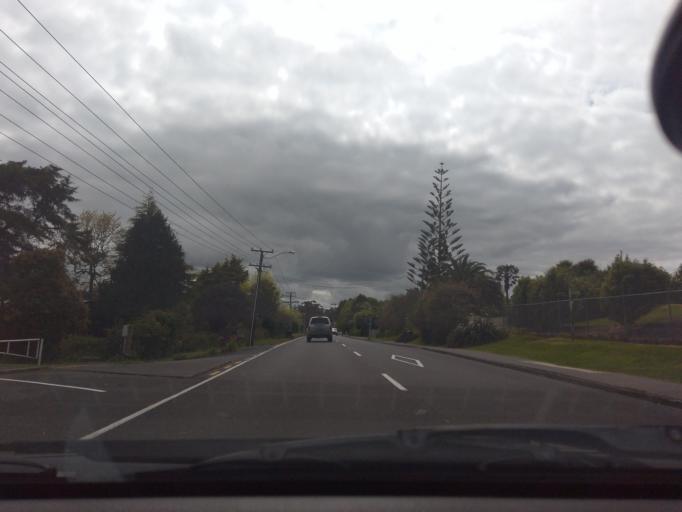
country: NZ
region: Auckland
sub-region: Auckland
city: Muriwai Beach
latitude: -36.8516
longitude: 174.5401
